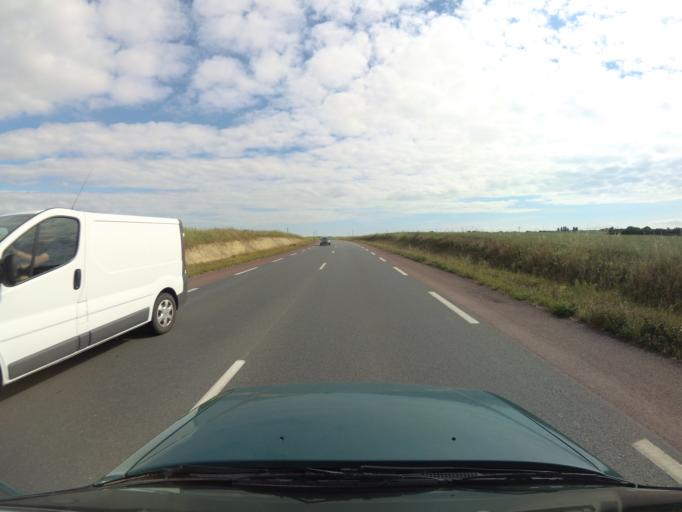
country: FR
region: Poitou-Charentes
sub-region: Departement de la Charente-Maritime
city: Saint-Xandre
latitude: 46.2139
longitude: -1.0909
